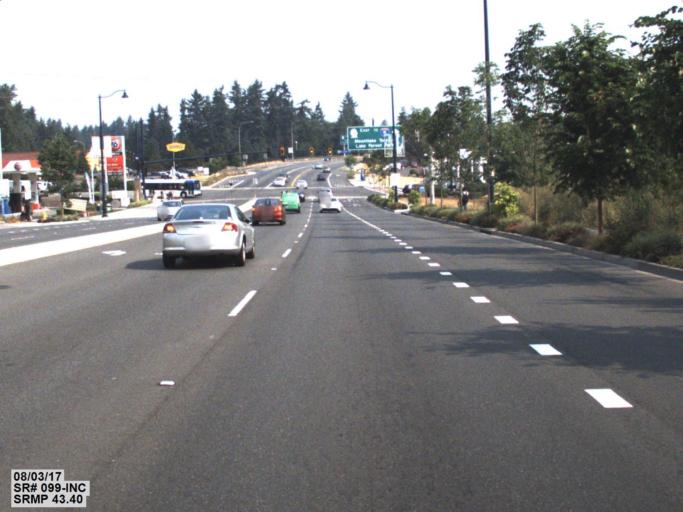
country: US
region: Washington
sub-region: Snohomish County
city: Esperance
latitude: 47.7765
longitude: -122.3461
